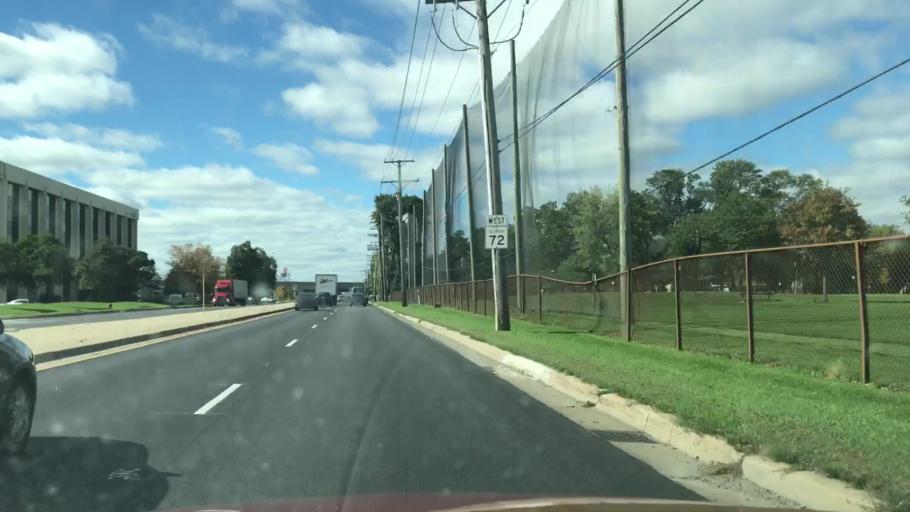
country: US
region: Illinois
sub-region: Cook County
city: Rosemont
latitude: 42.0094
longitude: -87.8973
